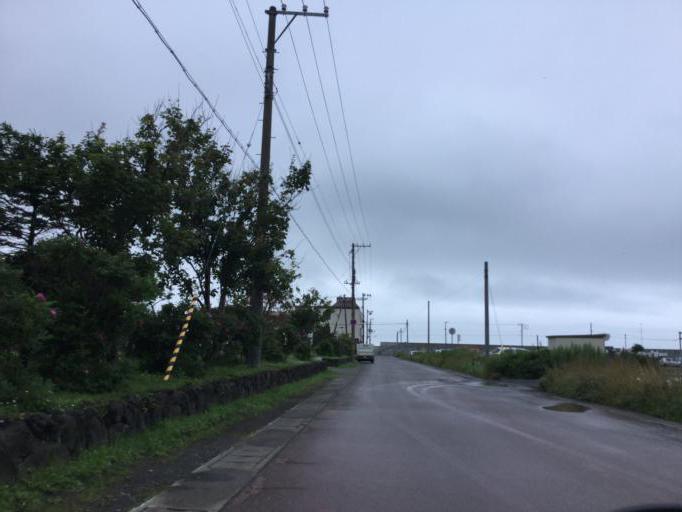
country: JP
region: Hokkaido
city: Wakkanai
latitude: 45.4187
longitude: 141.6769
